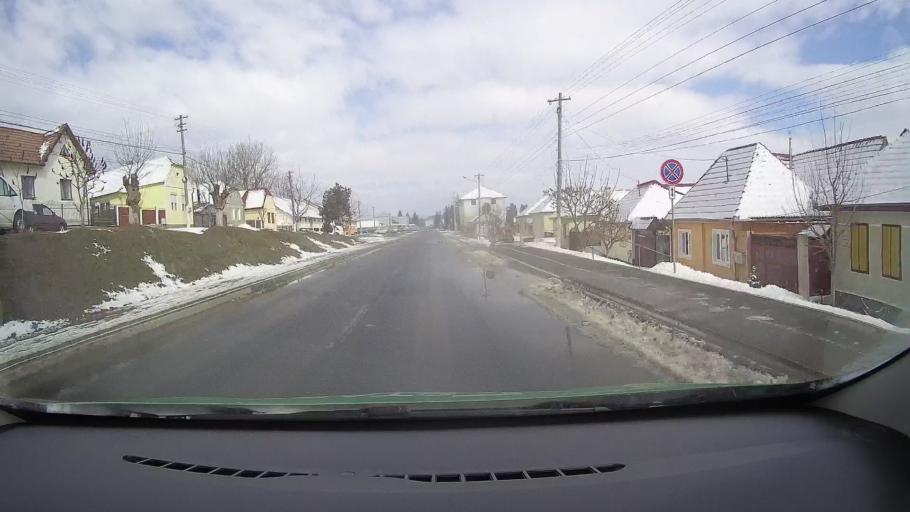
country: RO
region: Sibiu
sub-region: Oras Agnita
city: Agnita
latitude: 45.9801
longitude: 24.6366
